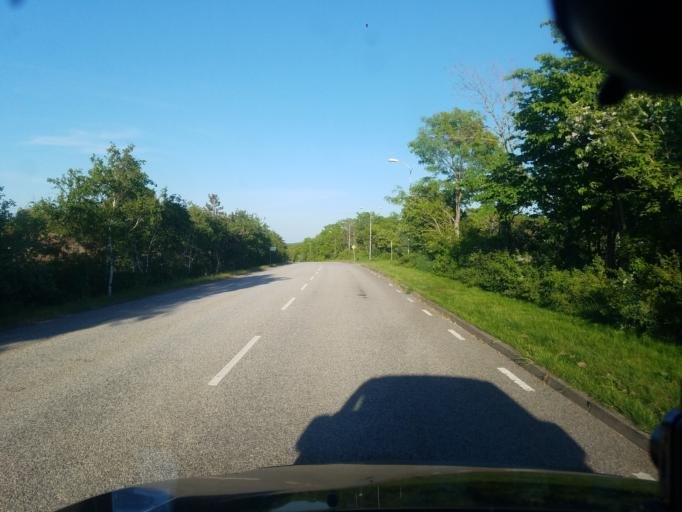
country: SE
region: Vaestra Goetaland
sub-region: Lysekils Kommun
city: Lysekil
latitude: 58.2863
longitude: 11.4529
